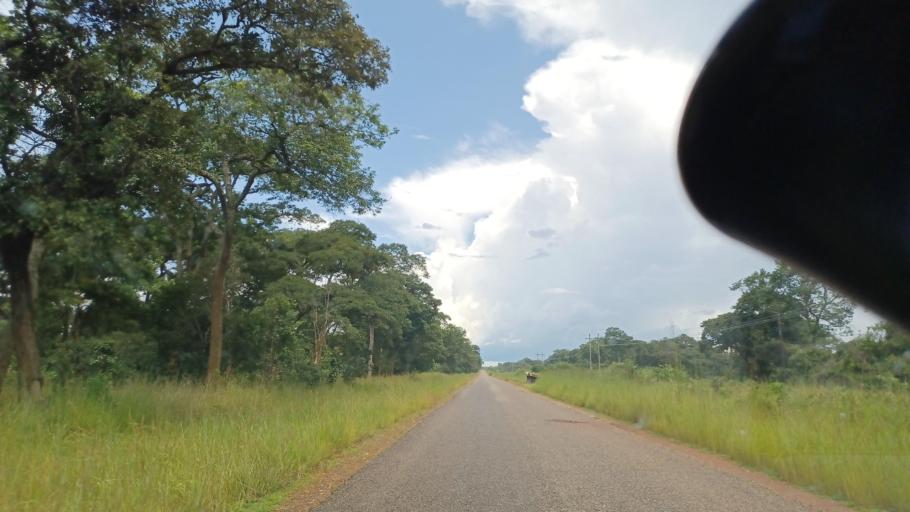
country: ZM
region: North-Western
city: Kasempa
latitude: -12.8879
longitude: 26.0492
